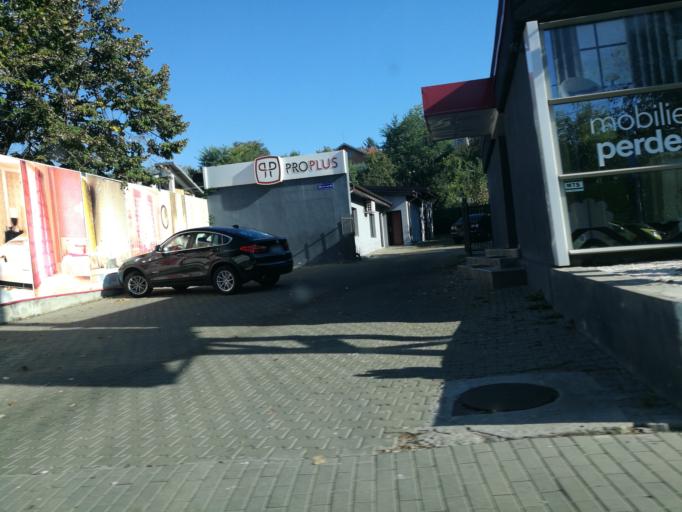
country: RO
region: Iasi
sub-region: Municipiul Iasi
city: Iasi
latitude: 47.1727
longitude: 27.5627
